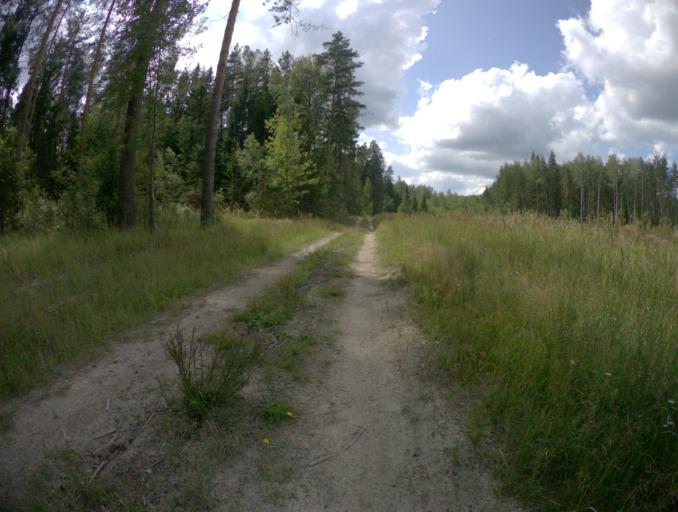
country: RU
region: Vladimir
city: Vorsha
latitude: 55.9658
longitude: 40.1694
